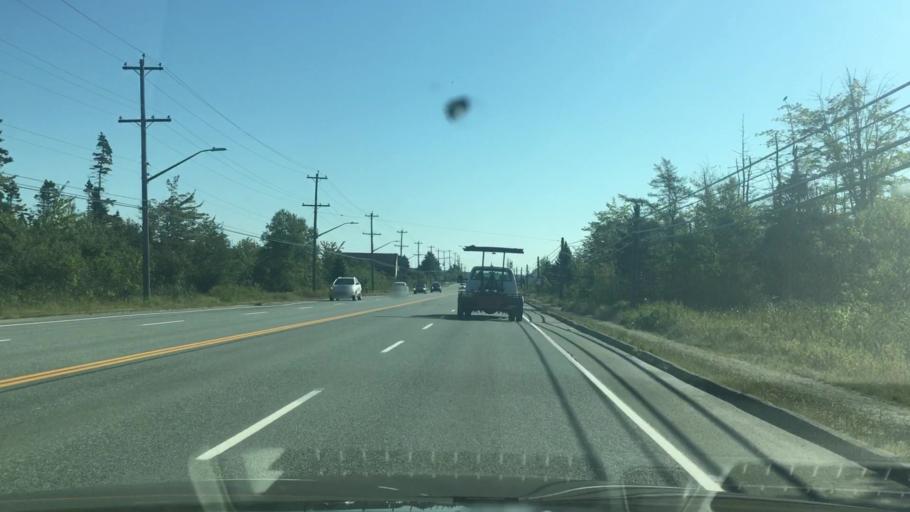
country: CA
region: Nova Scotia
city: Cole Harbour
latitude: 44.7019
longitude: -63.4759
